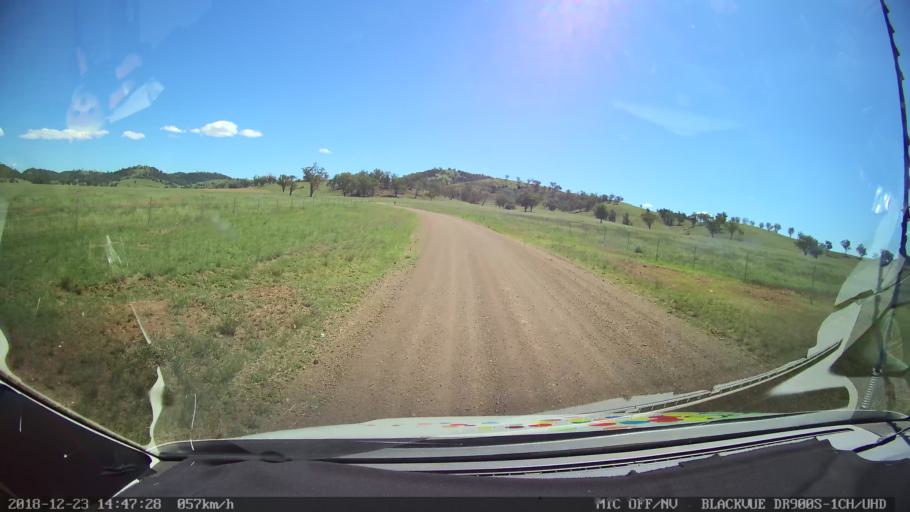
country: AU
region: New South Wales
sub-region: Tamworth Municipality
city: Manilla
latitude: -30.6541
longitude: 150.8742
